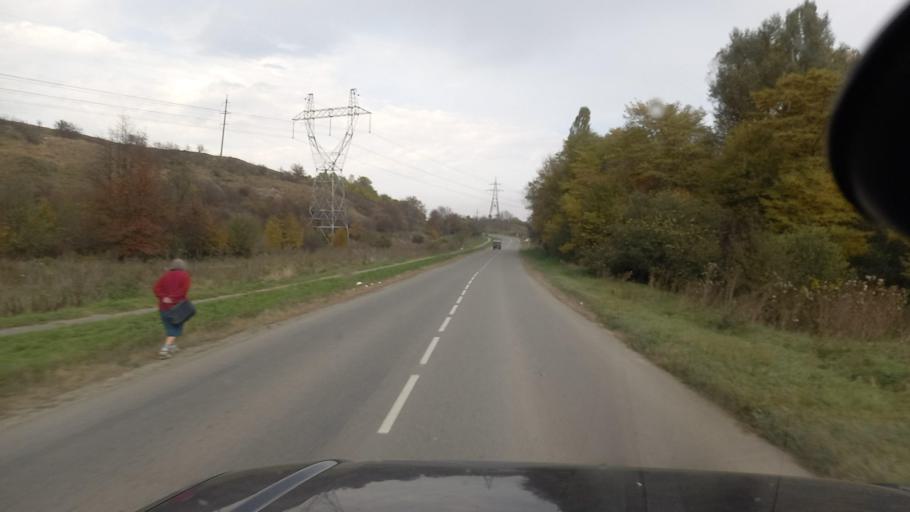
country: RU
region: Krasnodarskiy
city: Psebay
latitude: 44.1612
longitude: 40.8377
